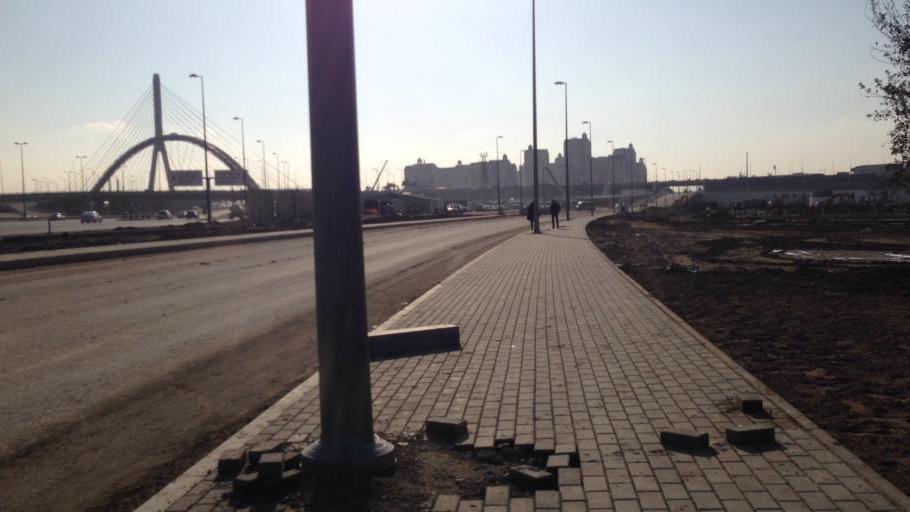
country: AZ
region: Baki
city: Sabuncu
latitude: 40.4282
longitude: 49.9233
